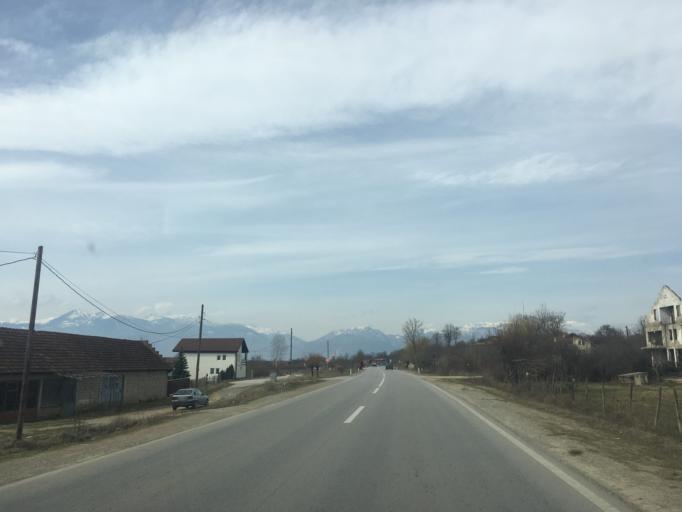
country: XK
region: Pec
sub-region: Komuna e Pejes
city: Kosuriq
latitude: 42.6160
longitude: 20.4962
